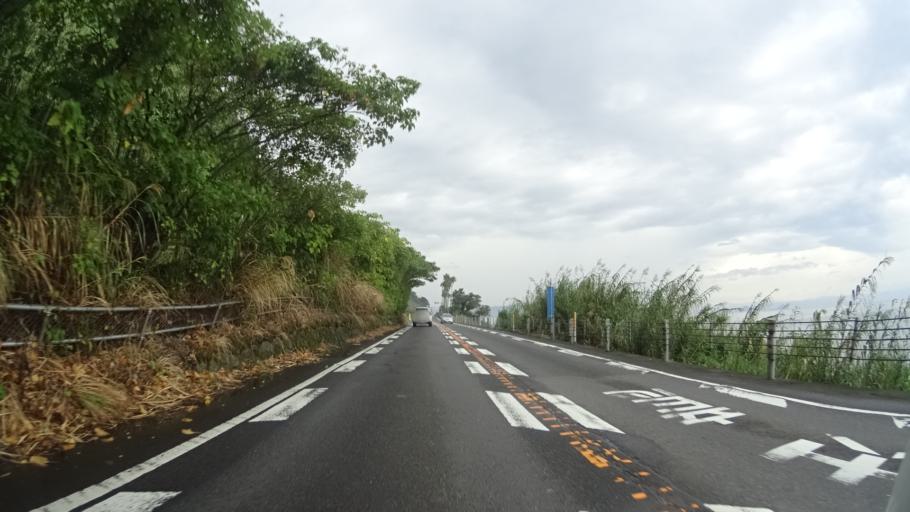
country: JP
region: Kagoshima
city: Kajiki
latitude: 31.6872
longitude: 130.6111
